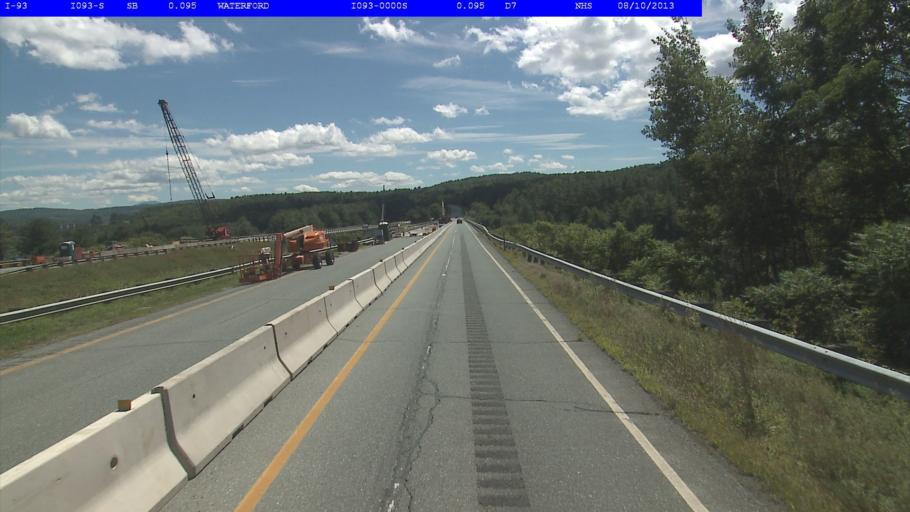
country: US
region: New Hampshire
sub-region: Grafton County
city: Littleton
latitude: 44.3445
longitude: -71.8918
